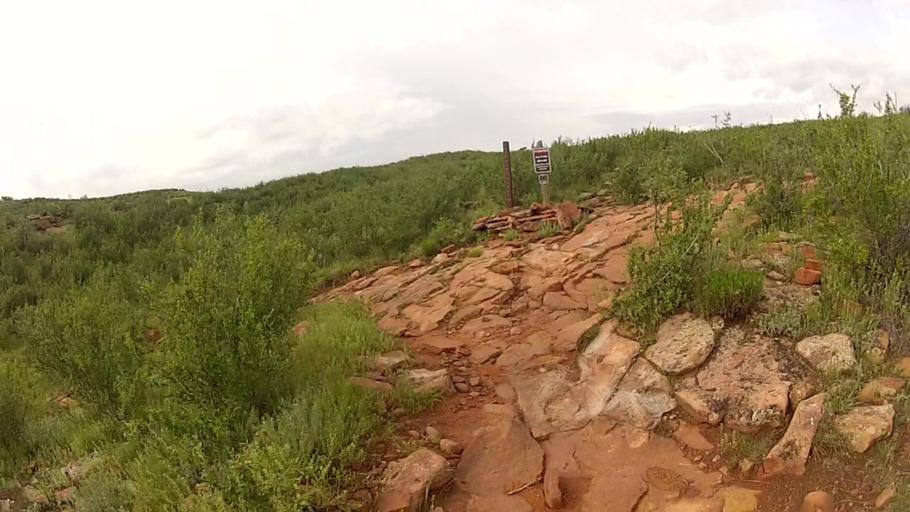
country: US
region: Colorado
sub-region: Larimer County
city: Loveland
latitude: 40.4433
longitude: -105.1540
